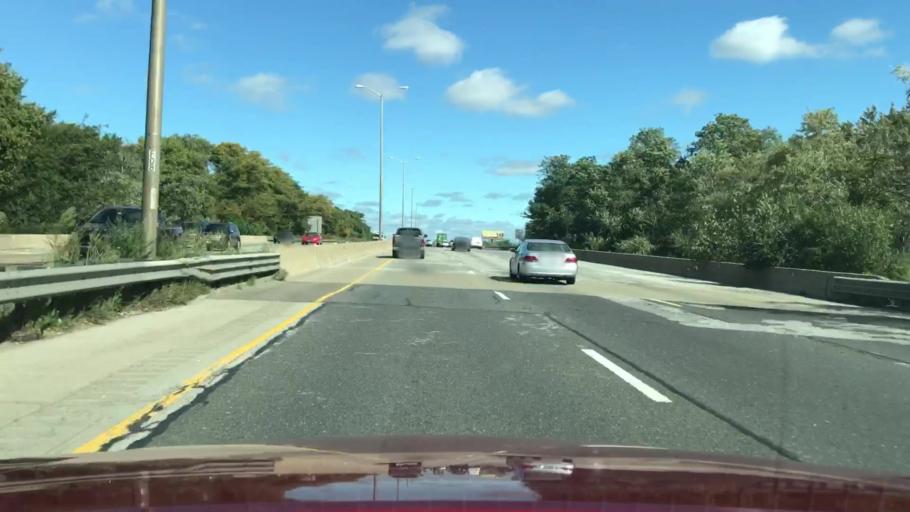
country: US
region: Illinois
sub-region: Cook County
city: South Holland
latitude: 41.6061
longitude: -87.5824
